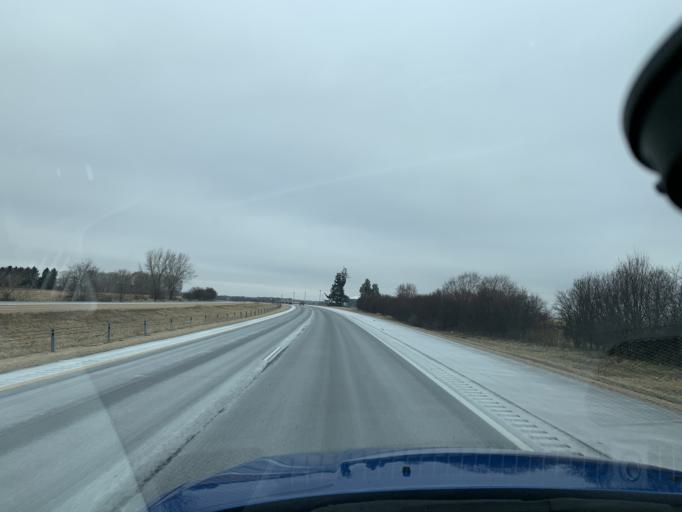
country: US
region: Wisconsin
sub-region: Dane County
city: Sun Prairie
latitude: 43.2126
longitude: -89.1684
